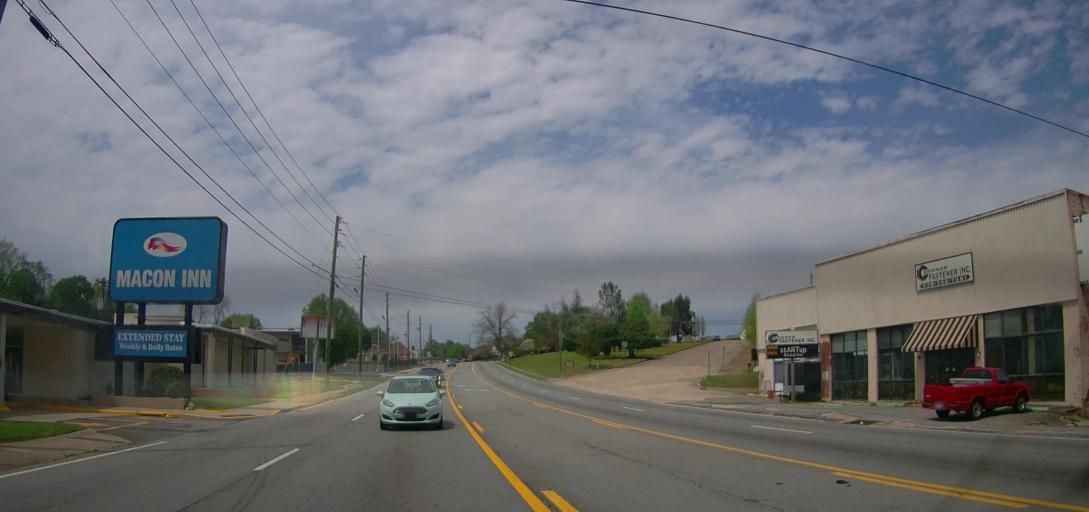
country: US
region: Georgia
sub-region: Bibb County
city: Macon
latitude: 32.8446
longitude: -83.6325
